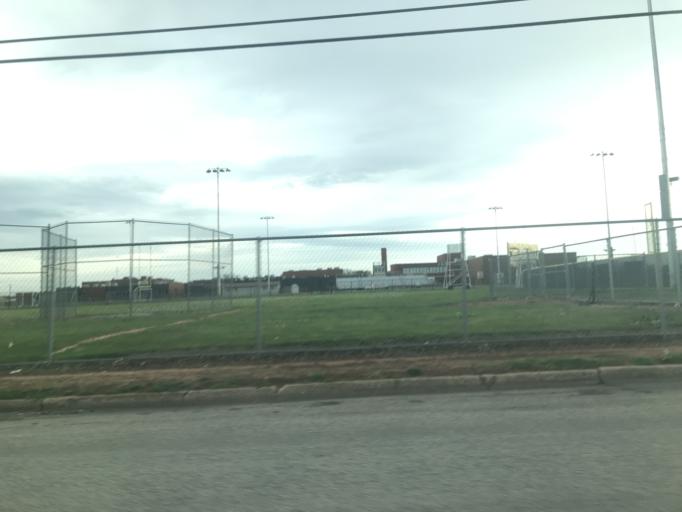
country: US
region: Texas
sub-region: Taylor County
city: Abilene
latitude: 32.4590
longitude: -99.7564
